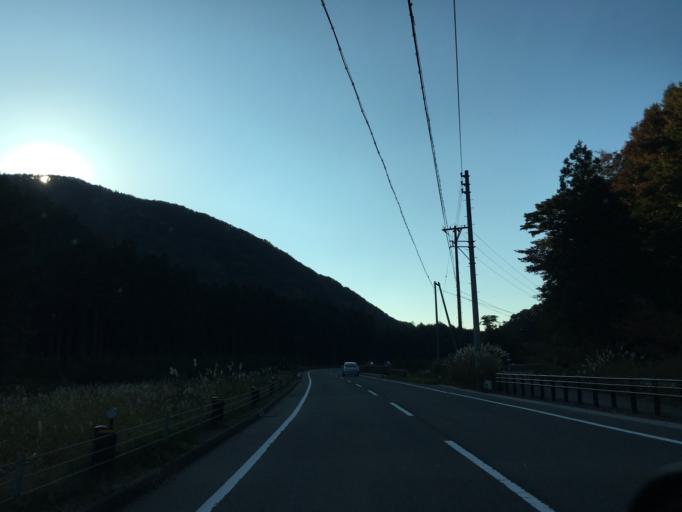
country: JP
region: Fukushima
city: Inawashiro
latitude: 37.3963
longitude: 140.1642
